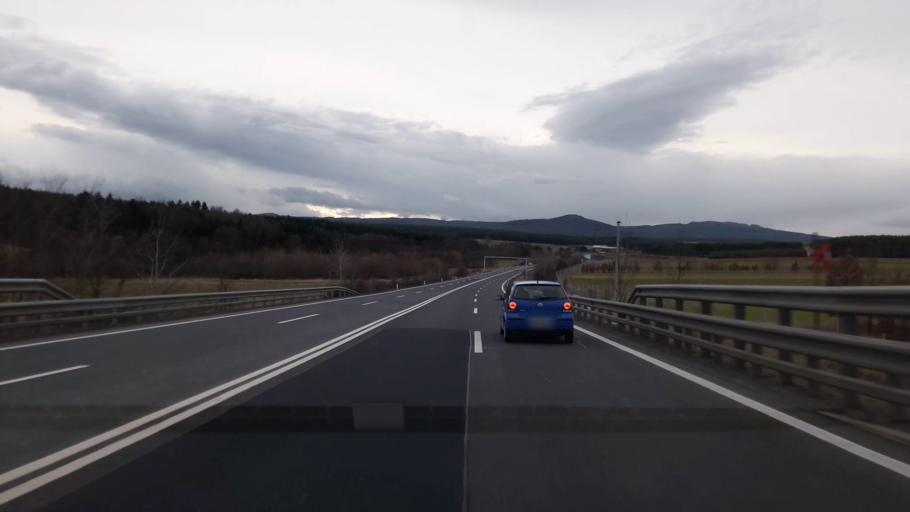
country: AT
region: Burgenland
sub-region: Politischer Bezirk Oberpullendorf
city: Neutal
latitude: 47.5281
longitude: 16.4495
